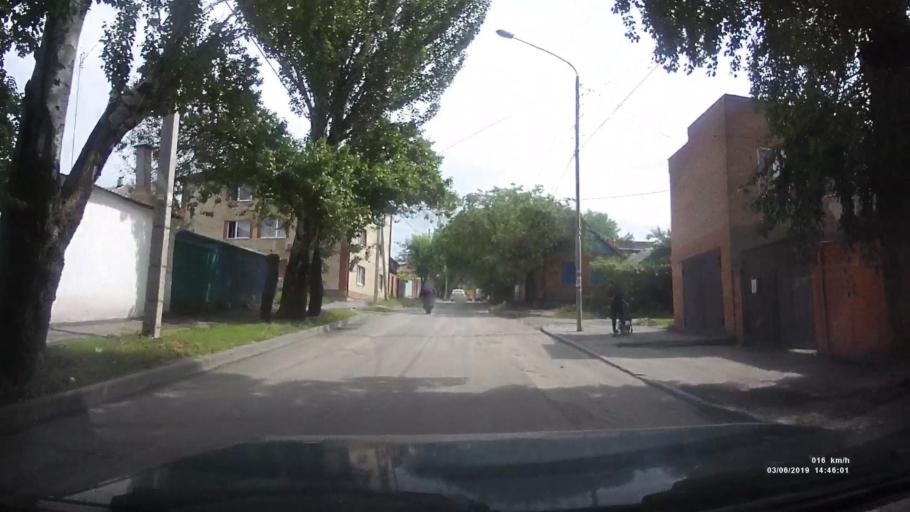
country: RU
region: Rostov
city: Rostov-na-Donu
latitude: 47.2463
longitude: 39.7239
